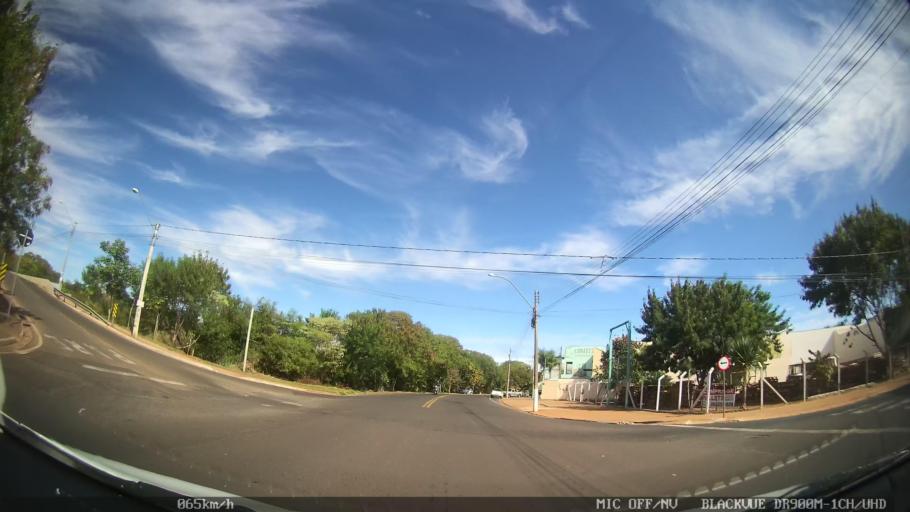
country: BR
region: Sao Paulo
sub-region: Sao Jose Do Rio Preto
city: Sao Jose do Rio Preto
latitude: -20.8451
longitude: -49.3594
